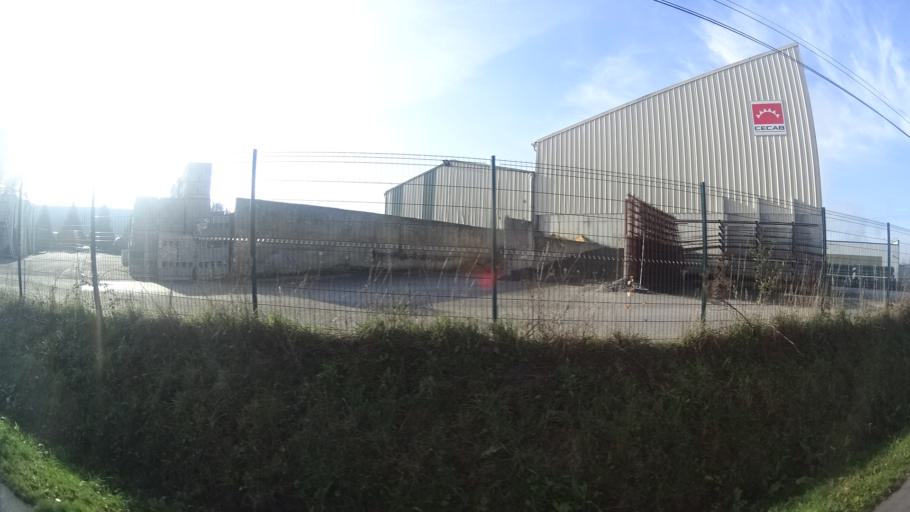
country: FR
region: Brittany
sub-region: Departement du Morbihan
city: Allaire
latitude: 47.6289
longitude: -2.1623
